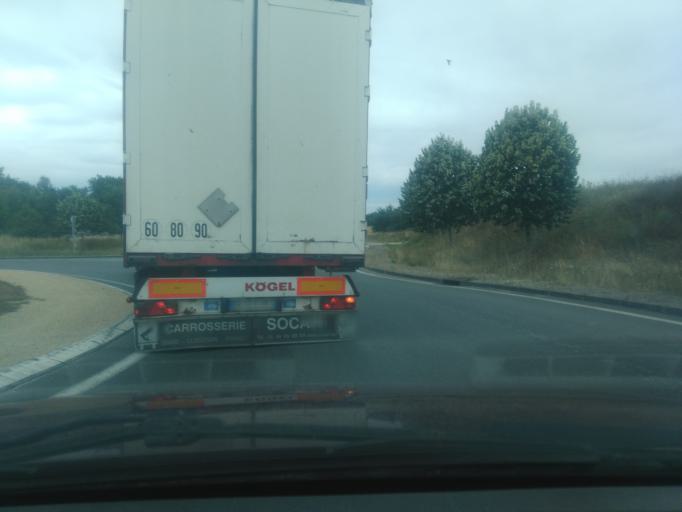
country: FR
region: Poitou-Charentes
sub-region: Departement de la Vienne
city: Chauvigny
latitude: 46.5623
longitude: 0.6182
